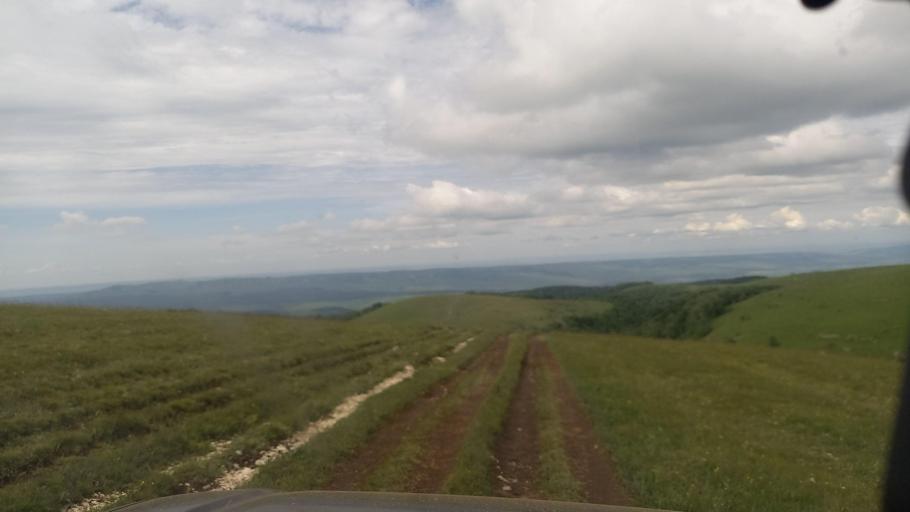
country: RU
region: Karachayevo-Cherkesiya
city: Pregradnaya
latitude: 43.9958
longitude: 41.2719
